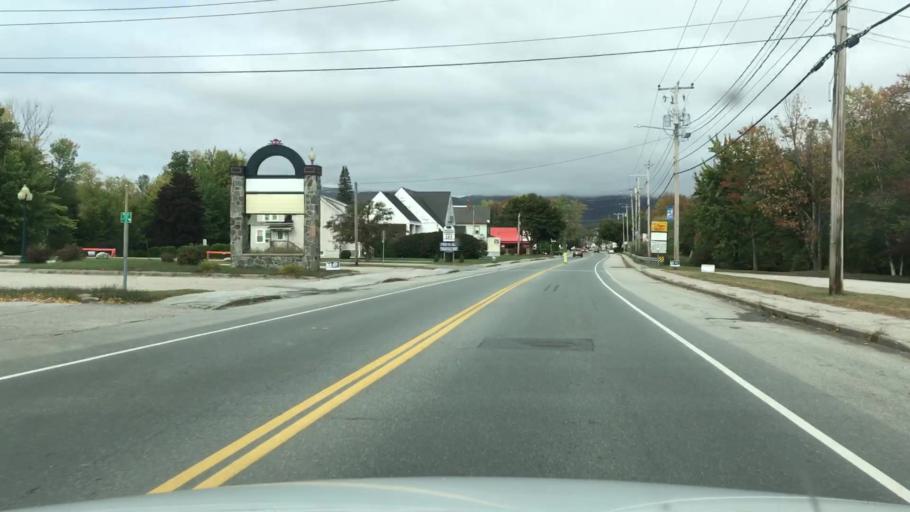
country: US
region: New Hampshire
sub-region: Coos County
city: Gorham
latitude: 44.3906
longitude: -71.1822
